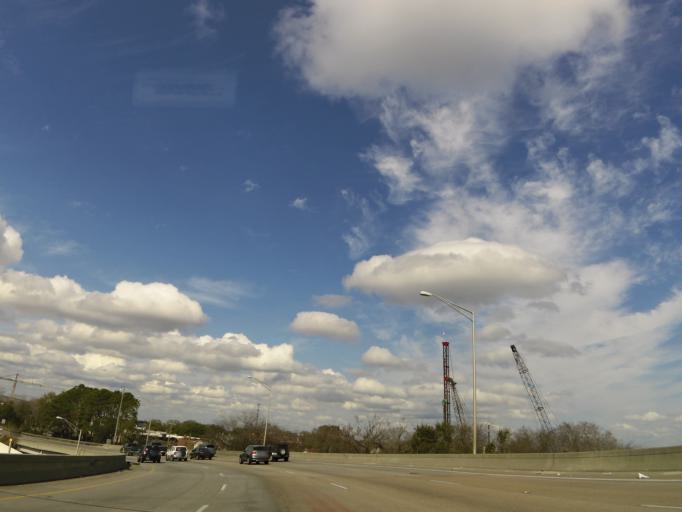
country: US
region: South Carolina
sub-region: Charleston County
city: Charleston
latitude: 32.7964
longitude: -79.9424
